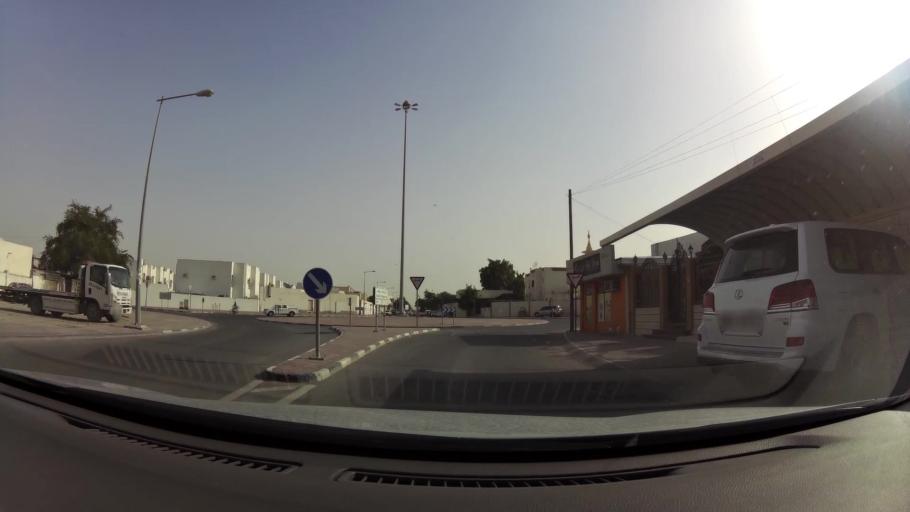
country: QA
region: Baladiyat ar Rayyan
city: Ar Rayyan
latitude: 25.2373
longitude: 51.4367
